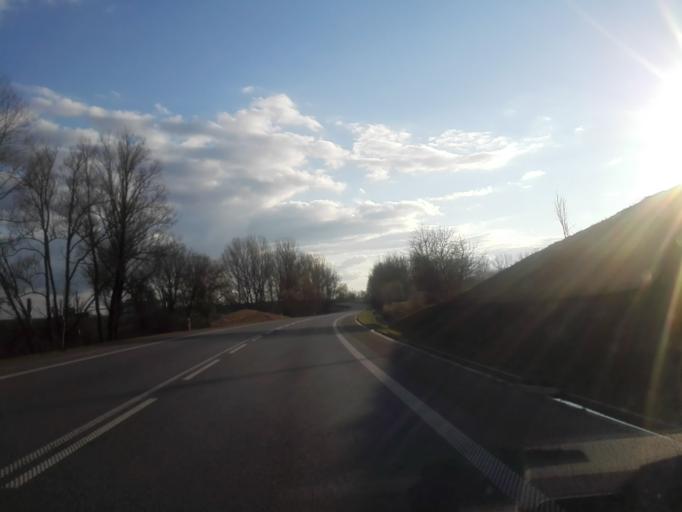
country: PL
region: Podlasie
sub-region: Suwalki
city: Suwalki
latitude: 54.1975
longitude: 23.0183
